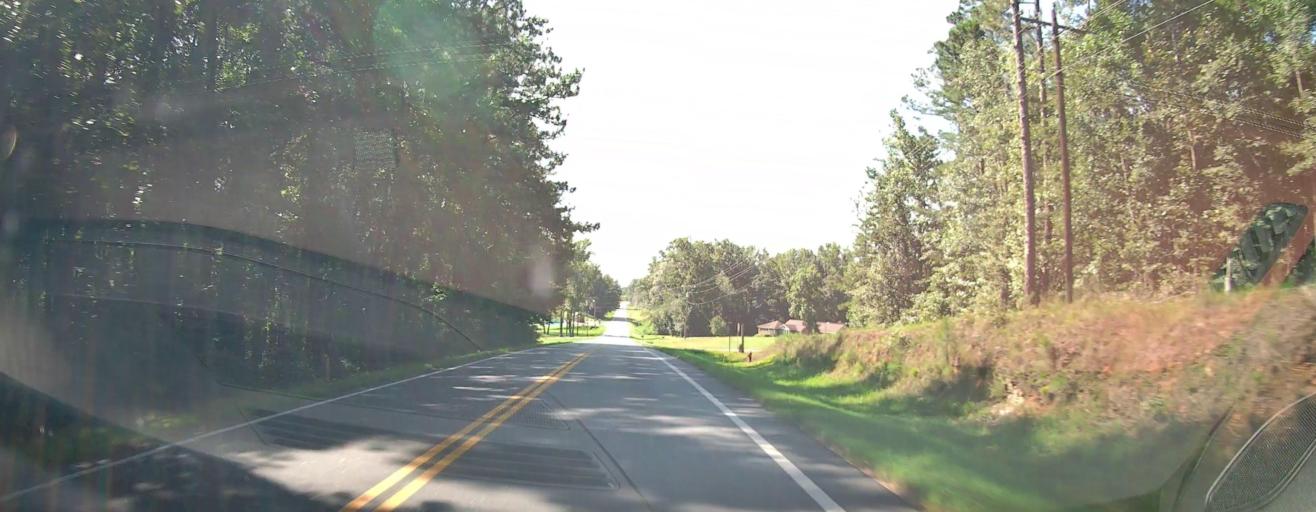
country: US
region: Georgia
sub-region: Upson County
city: Hannahs Mill
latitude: 32.9166
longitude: -84.4308
